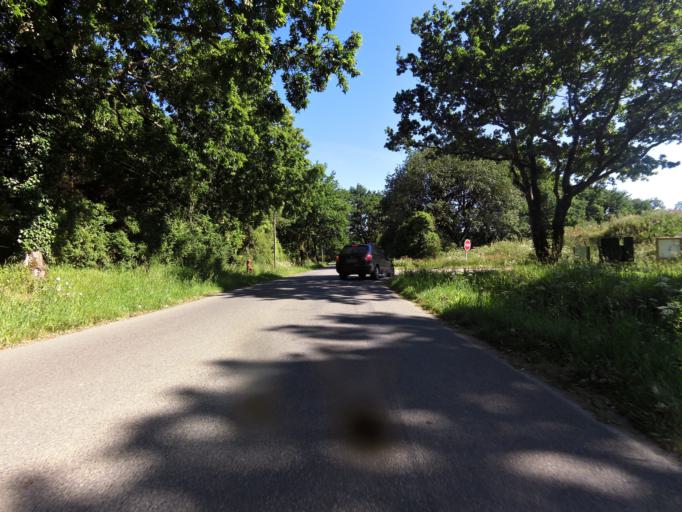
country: FR
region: Brittany
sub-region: Departement du Morbihan
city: Penestin
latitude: 47.4729
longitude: -2.4605
